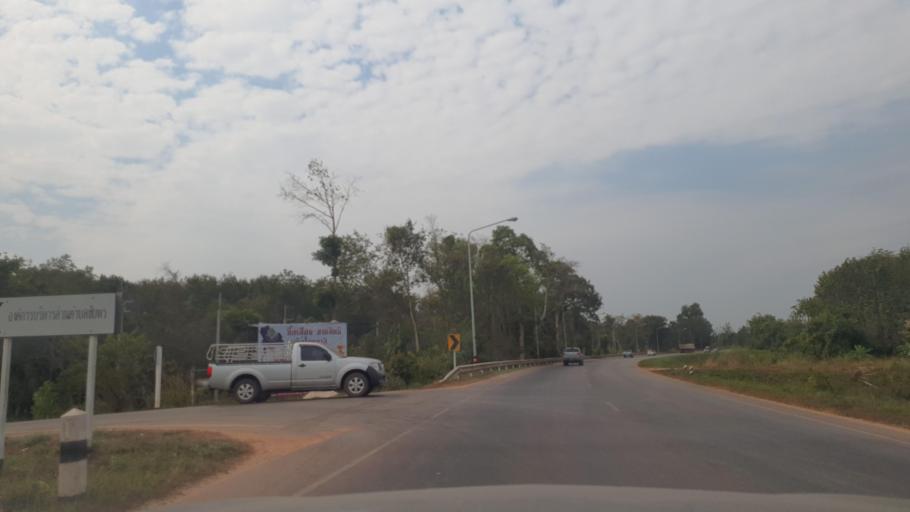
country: TH
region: Changwat Bueng Kan
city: Si Wilai
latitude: 18.2717
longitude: 103.8391
